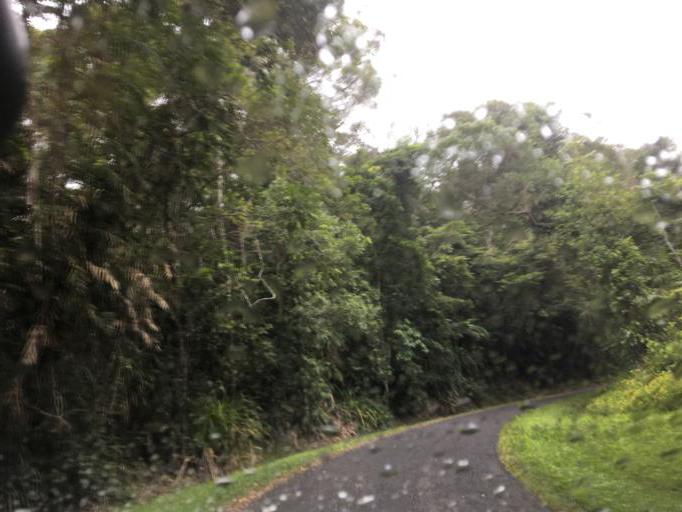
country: AU
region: Queensland
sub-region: Tablelands
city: Kuranda
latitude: -16.8394
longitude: 145.6412
